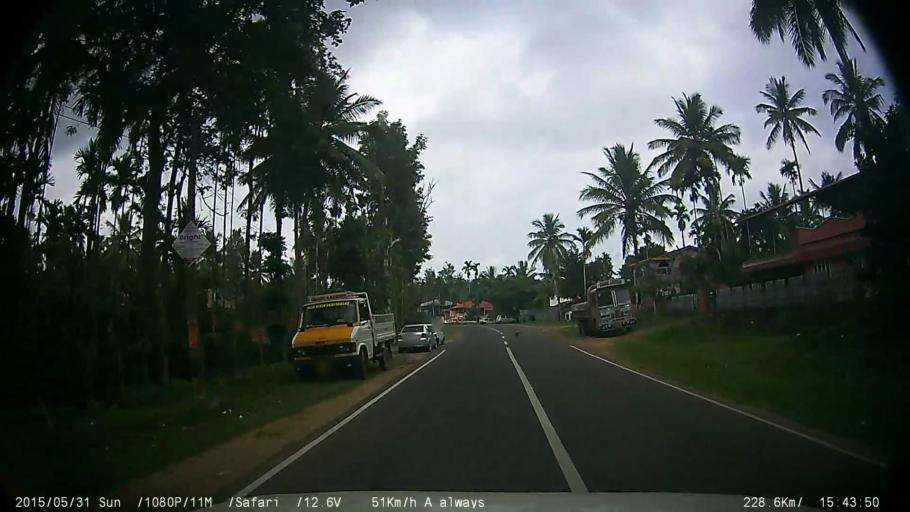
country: IN
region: Kerala
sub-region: Wayanad
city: Panamaram
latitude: 11.6726
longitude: 76.2818
